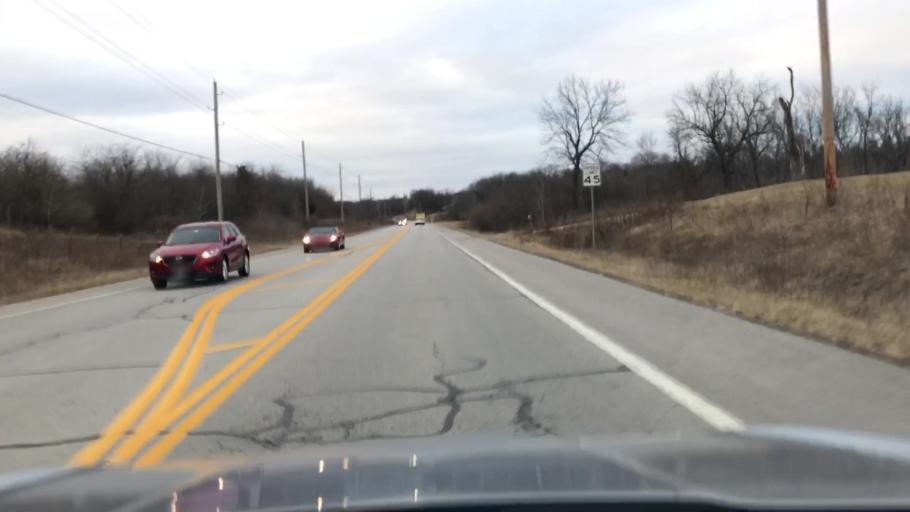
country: US
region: Missouri
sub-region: Jackson County
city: Lees Summit
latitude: 38.8981
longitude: -94.4144
